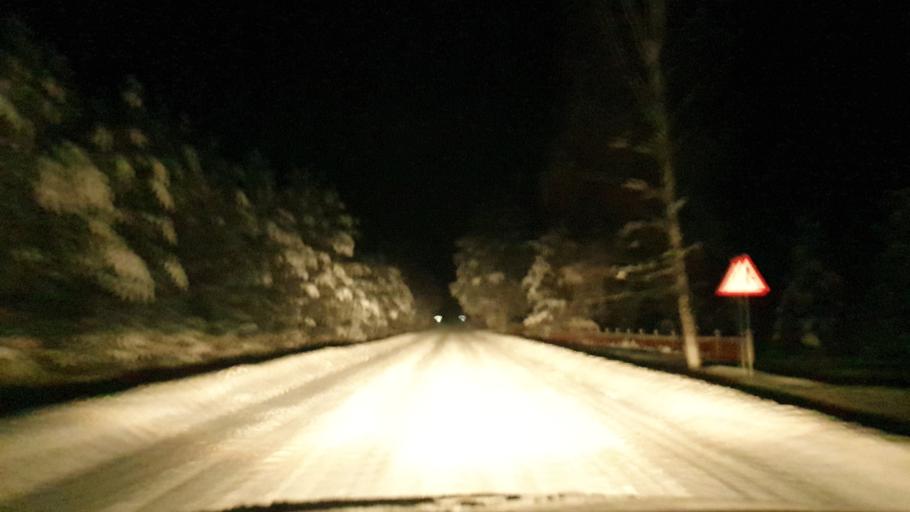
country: EE
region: Vorumaa
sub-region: Antsla vald
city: Vana-Antsla
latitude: 57.9585
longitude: 26.6606
